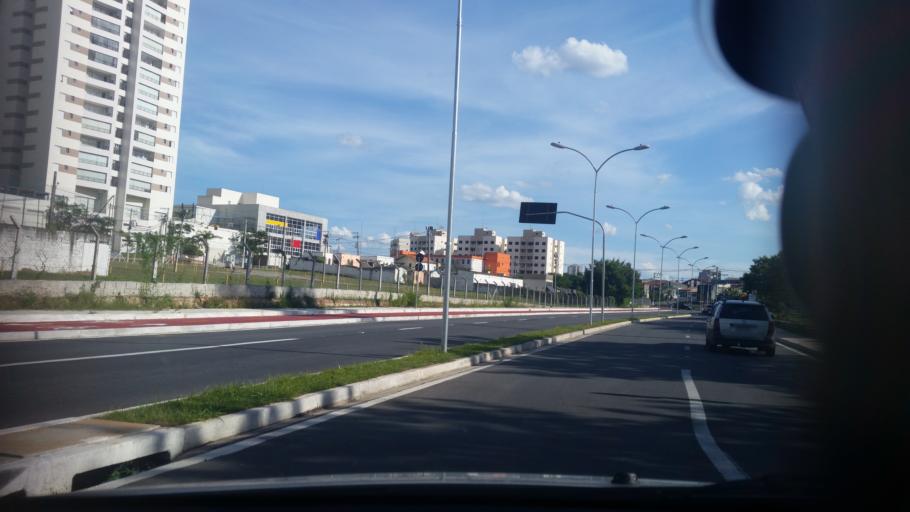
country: BR
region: Sao Paulo
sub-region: Taubate
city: Taubate
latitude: -23.0230
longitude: -45.5735
